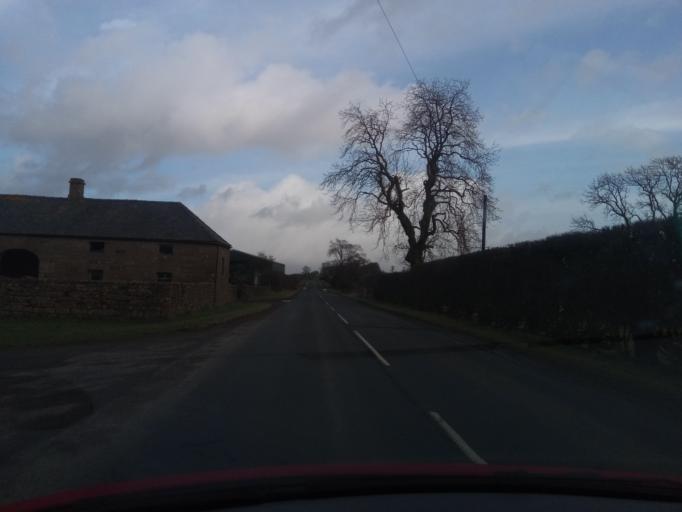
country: GB
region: England
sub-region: Northumberland
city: Rothley
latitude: 55.1248
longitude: -2.0006
